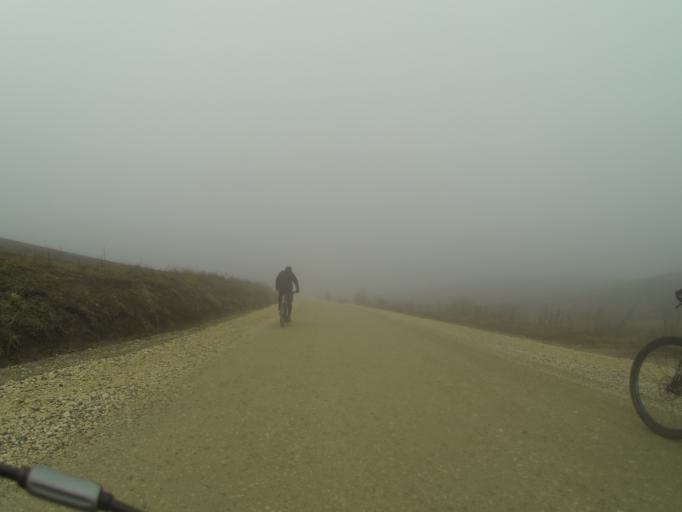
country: RO
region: Mehedinti
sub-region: Comuna Balacita
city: Gvardinita
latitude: 44.4237
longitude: 23.1309
